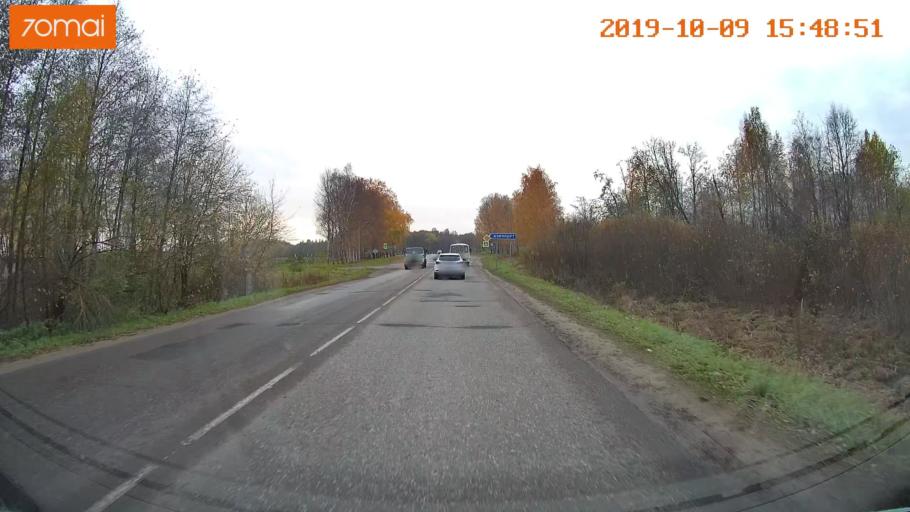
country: RU
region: Kostroma
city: Oktyabr'skiy
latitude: 57.8098
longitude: 41.0114
